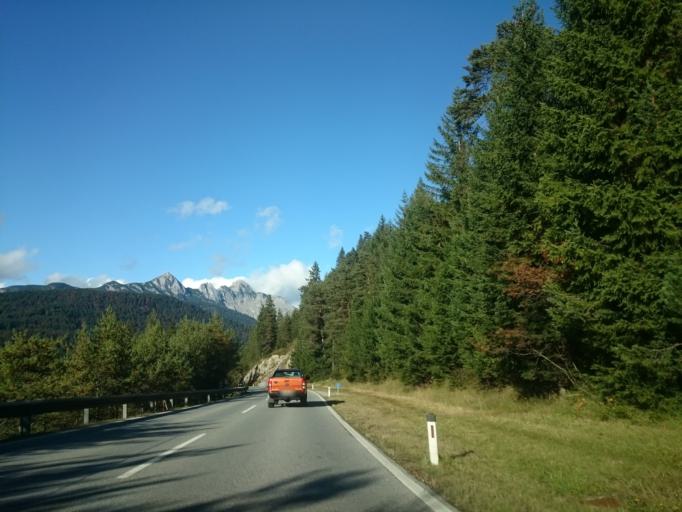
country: AT
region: Tyrol
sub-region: Politischer Bezirk Innsbruck Land
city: Seefeld in Tirol
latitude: 47.3364
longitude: 11.1960
